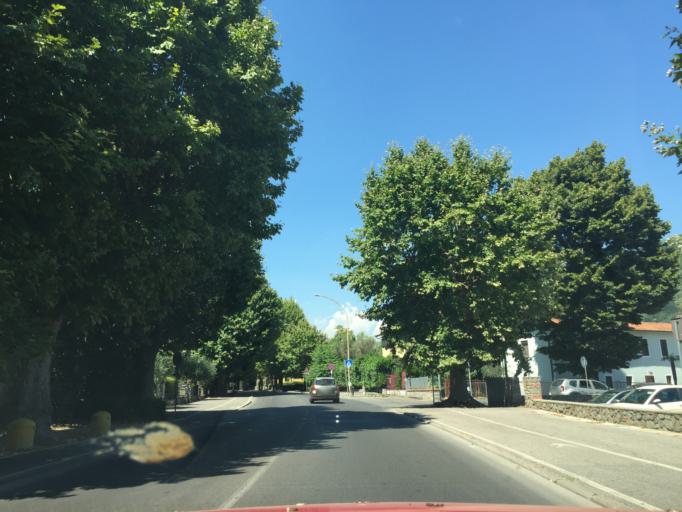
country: IT
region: Tuscany
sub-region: Provincia di Pistoia
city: Pescia
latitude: 43.8912
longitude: 10.6897
